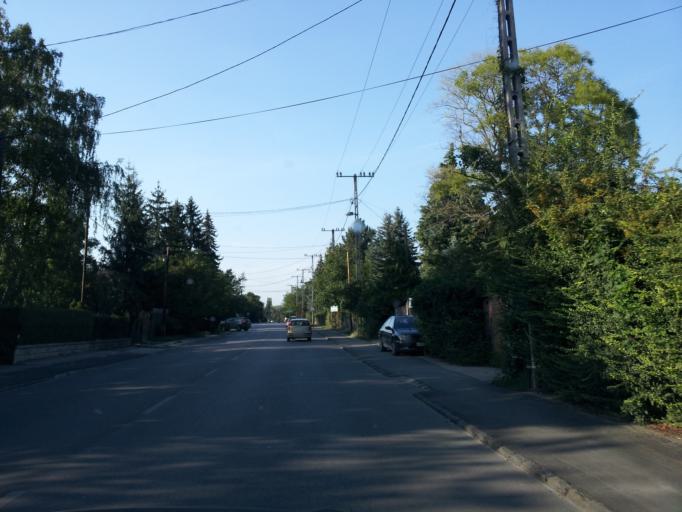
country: HU
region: Pest
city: Leanyfalu
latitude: 47.6965
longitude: 19.0884
